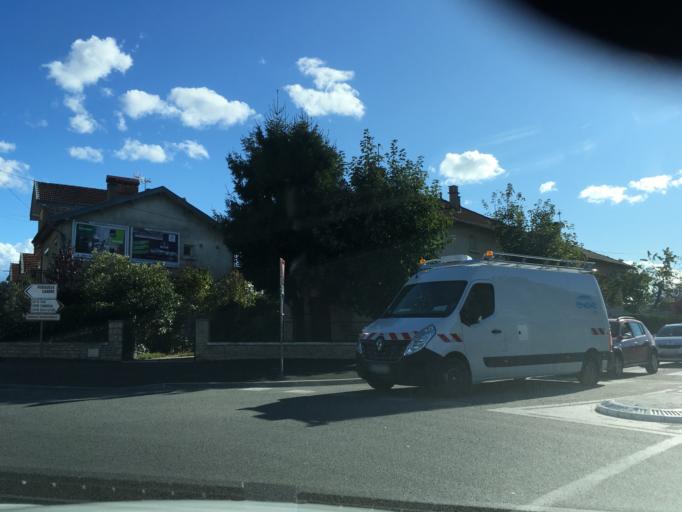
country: FR
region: Limousin
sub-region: Departement de la Correze
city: Brive-la-Gaillarde
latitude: 45.1565
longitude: 1.5041
